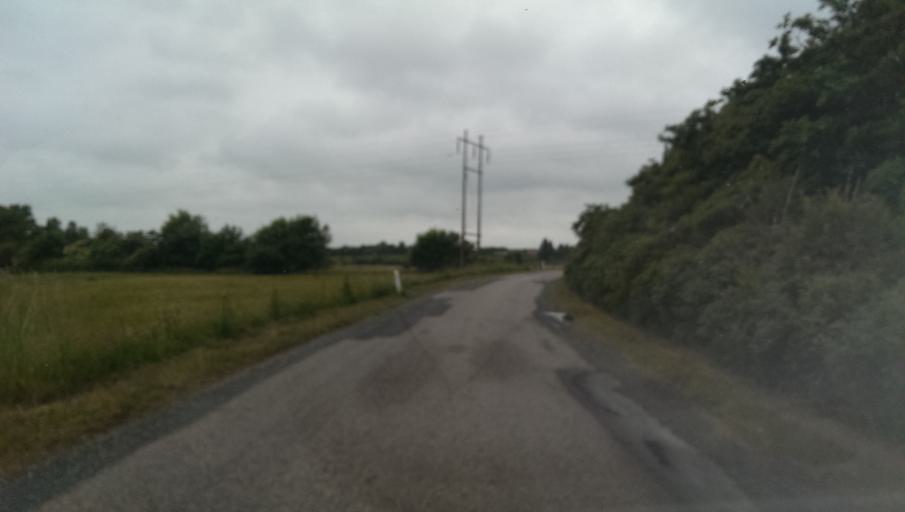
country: DK
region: South Denmark
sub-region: Esbjerg Kommune
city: Tjaereborg
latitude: 55.4711
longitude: 8.5897
